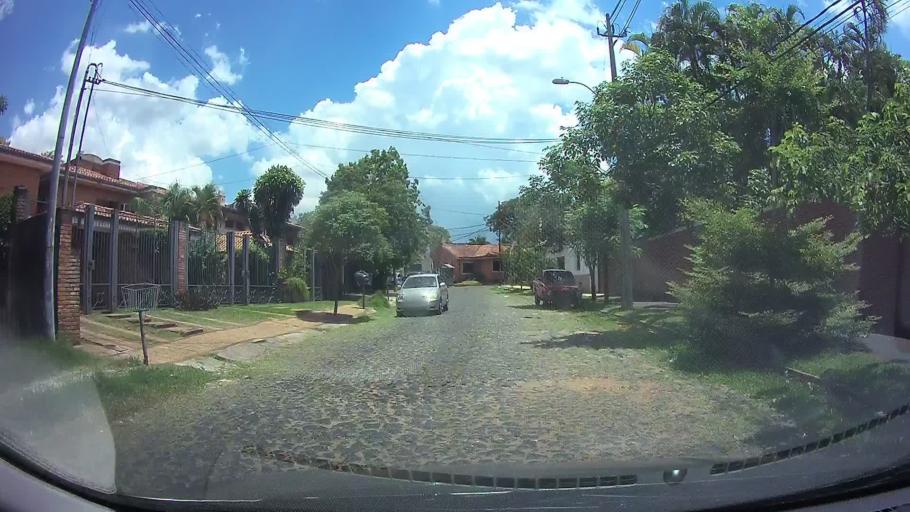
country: PY
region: Asuncion
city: Asuncion
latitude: -25.2970
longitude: -57.5973
